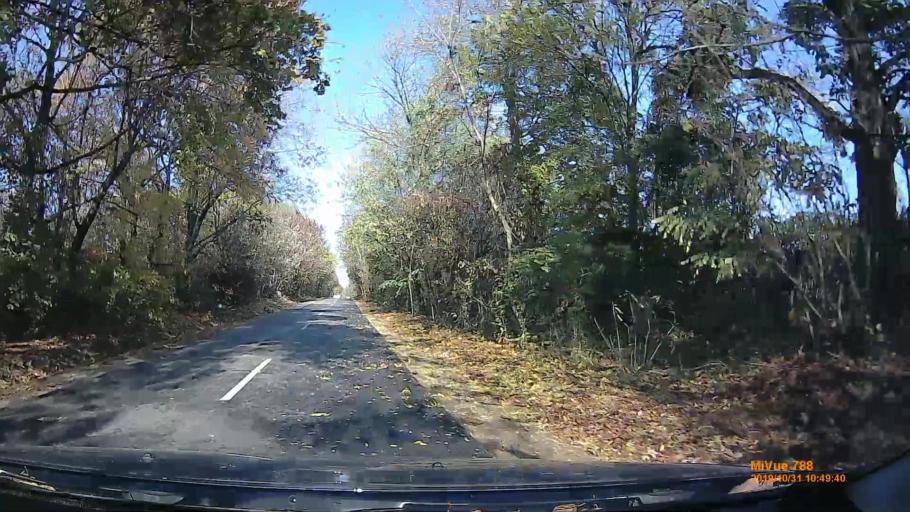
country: HU
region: Pest
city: Urom
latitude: 47.5928
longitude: 19.0024
